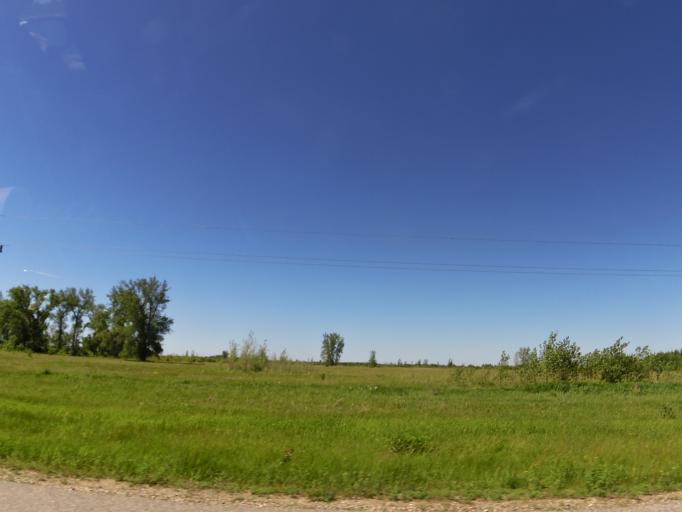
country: US
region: Minnesota
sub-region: Red Lake County
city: Red Lake Falls
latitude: 47.7280
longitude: -96.1984
